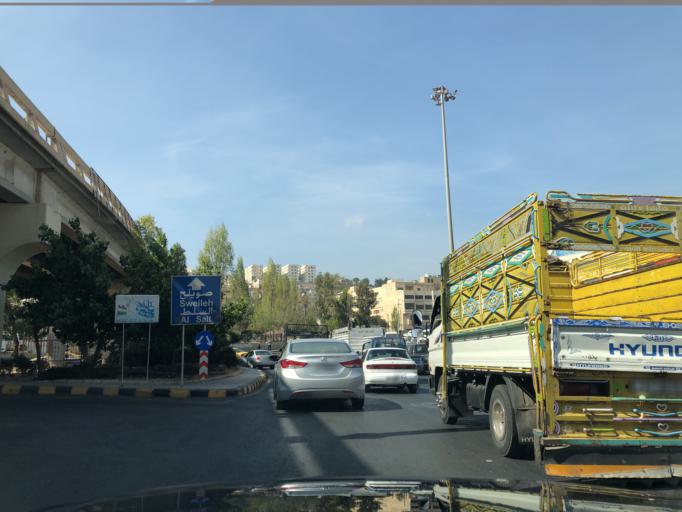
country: JO
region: Amman
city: Al Jubayhah
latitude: 32.0220
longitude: 35.8443
